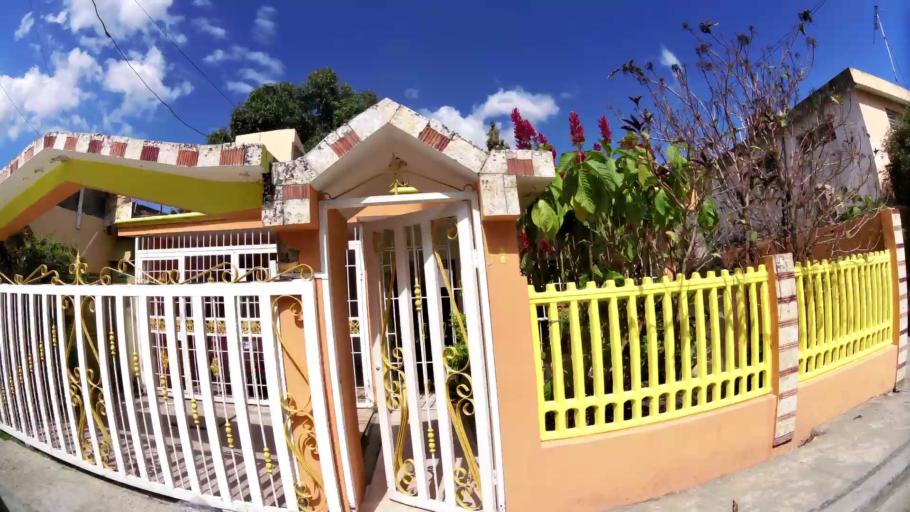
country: DO
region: San Cristobal
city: San Cristobal
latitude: 18.4239
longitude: -70.1041
